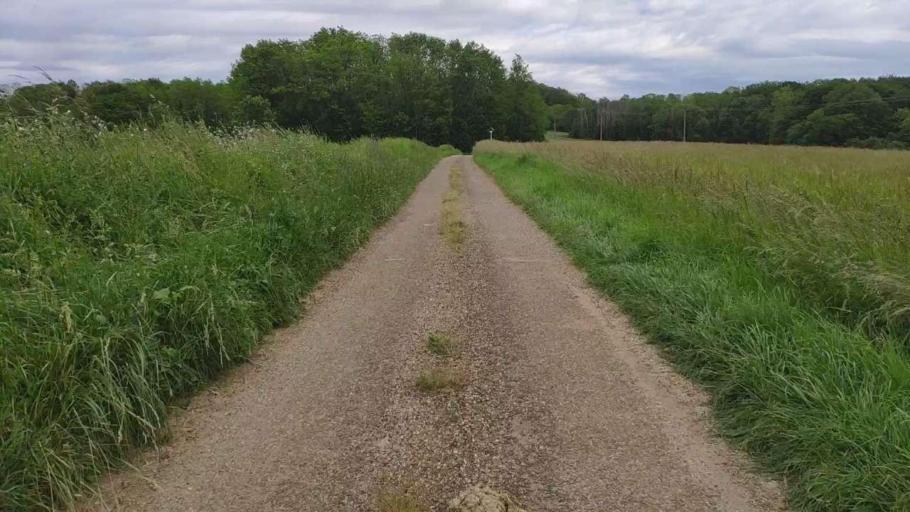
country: FR
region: Franche-Comte
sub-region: Departement du Jura
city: Bletterans
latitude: 46.7880
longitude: 5.5451
